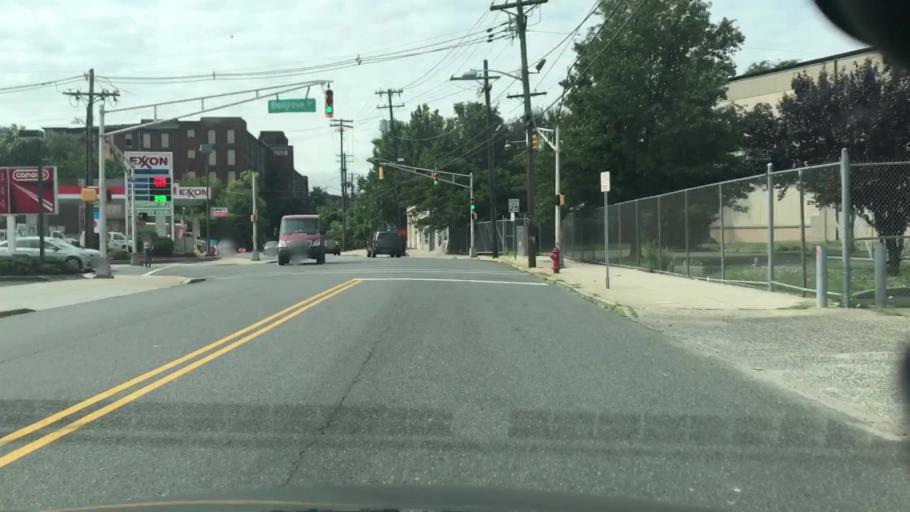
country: US
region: New Jersey
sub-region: Hudson County
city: East Newark
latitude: 40.7549
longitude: -74.1627
